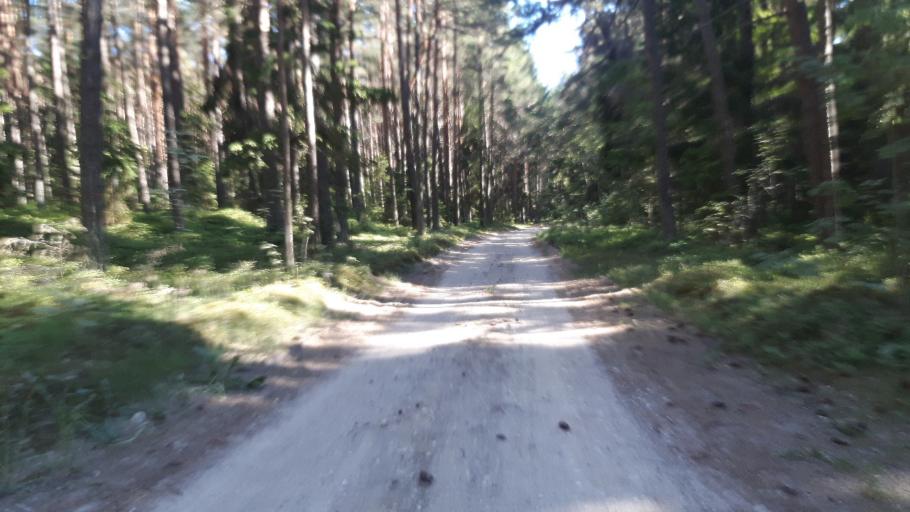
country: LV
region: Salacgrivas
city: Salacgriva
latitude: 57.7311
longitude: 24.3498
